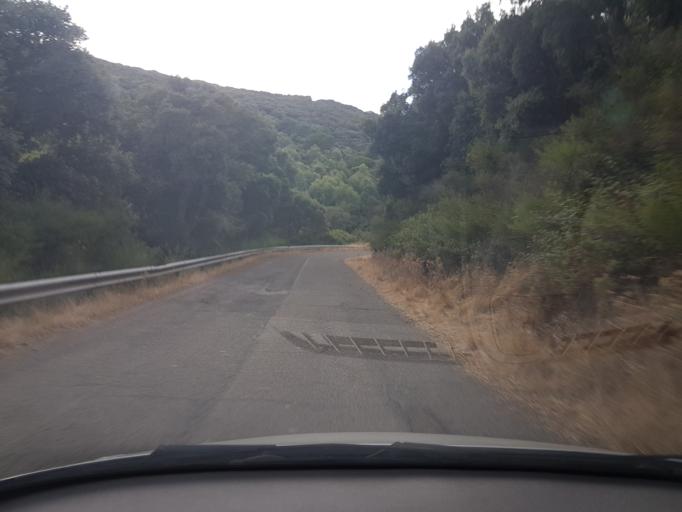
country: IT
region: Sardinia
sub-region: Provincia di Oristano
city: Seneghe
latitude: 40.1120
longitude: 8.6144
